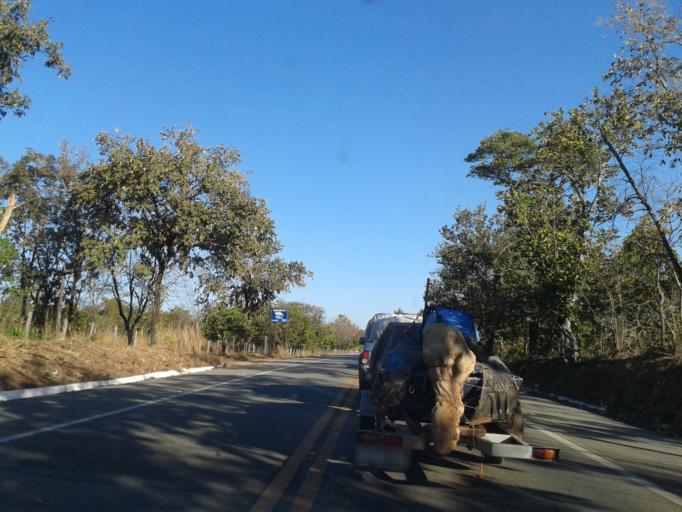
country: BR
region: Goias
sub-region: Itapuranga
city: Itapuranga
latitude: -15.5071
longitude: -50.3029
